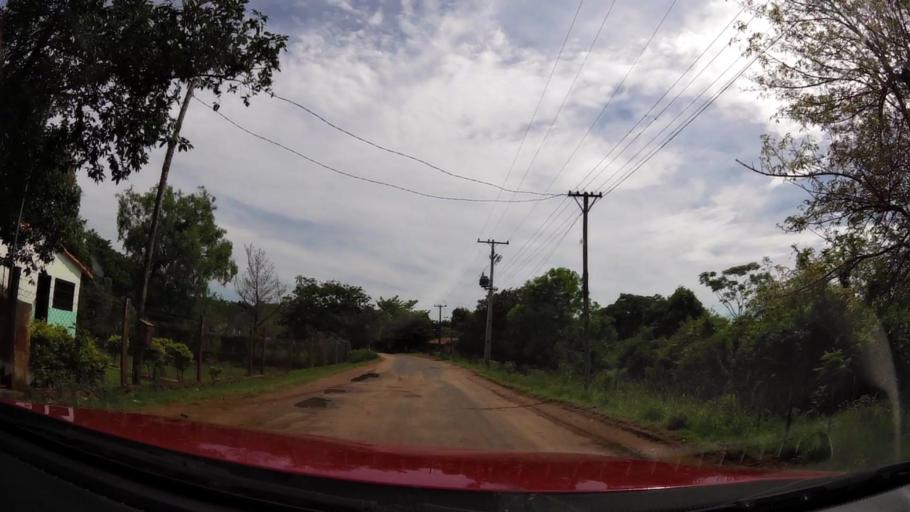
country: PY
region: Central
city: Limpio
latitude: -25.1758
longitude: -57.4418
